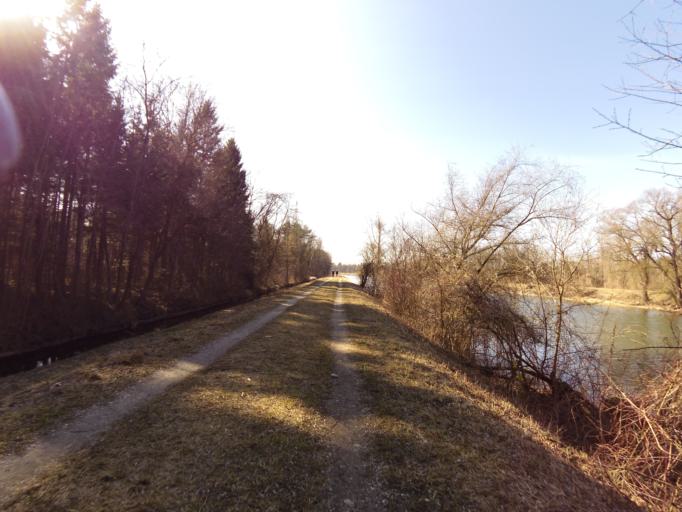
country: DE
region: Bavaria
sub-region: Lower Bavaria
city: Eching
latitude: 48.5004
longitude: 12.0282
